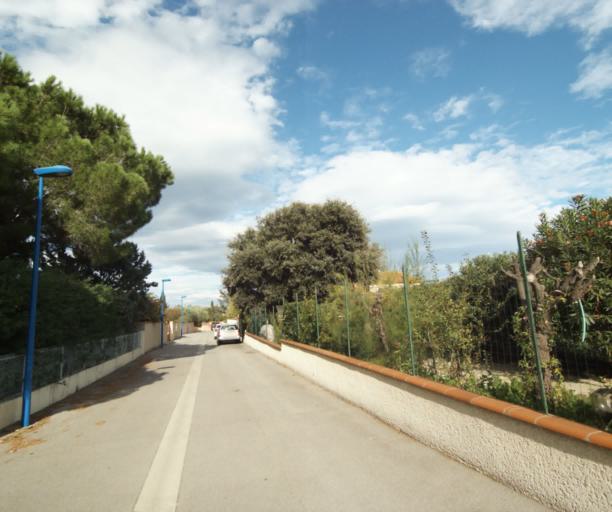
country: FR
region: Languedoc-Roussillon
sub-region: Departement des Pyrenees-Orientales
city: Argelers
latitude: 42.5458
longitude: 3.0131
